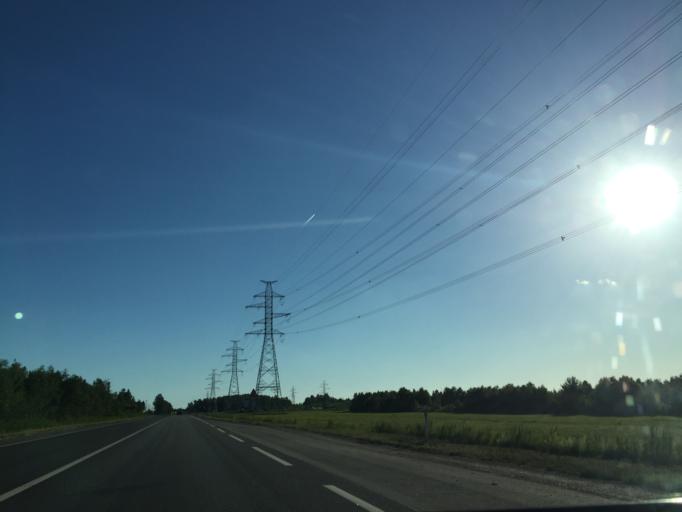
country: LV
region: Ventspils
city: Ventspils
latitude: 57.3990
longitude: 21.6551
